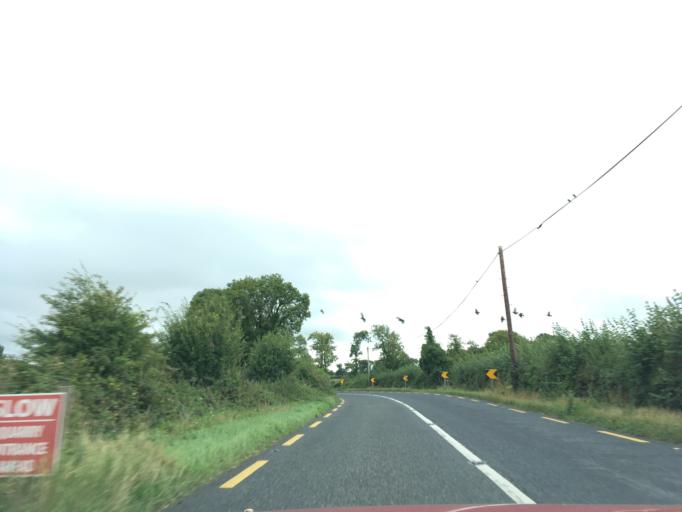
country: IE
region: Munster
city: Fethard
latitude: 52.4392
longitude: -7.7969
